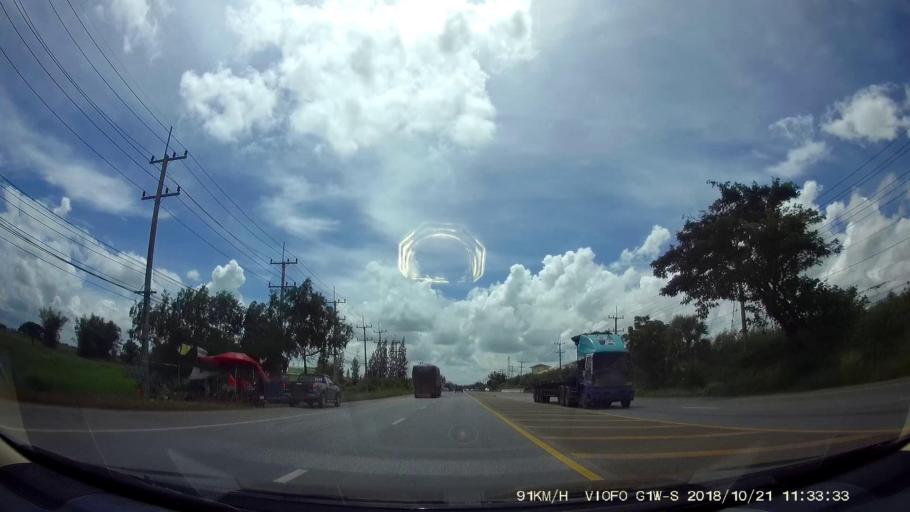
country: TH
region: Chaiyaphum
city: Chaiyaphum
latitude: 15.7442
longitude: 102.0242
